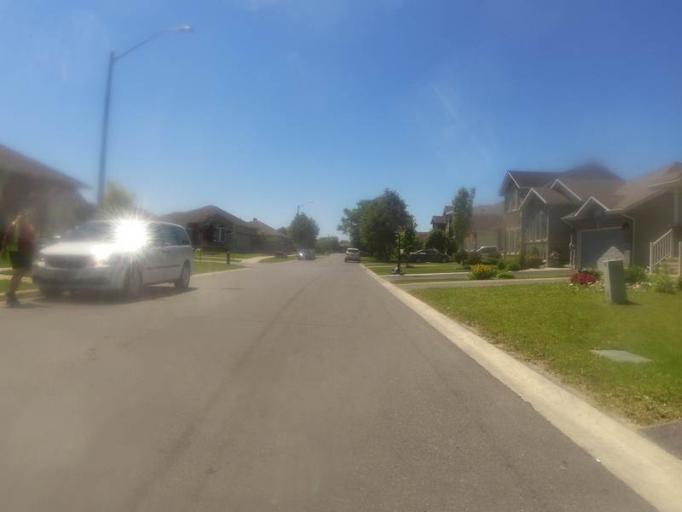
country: CA
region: Ontario
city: Kingston
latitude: 44.2639
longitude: -76.5561
